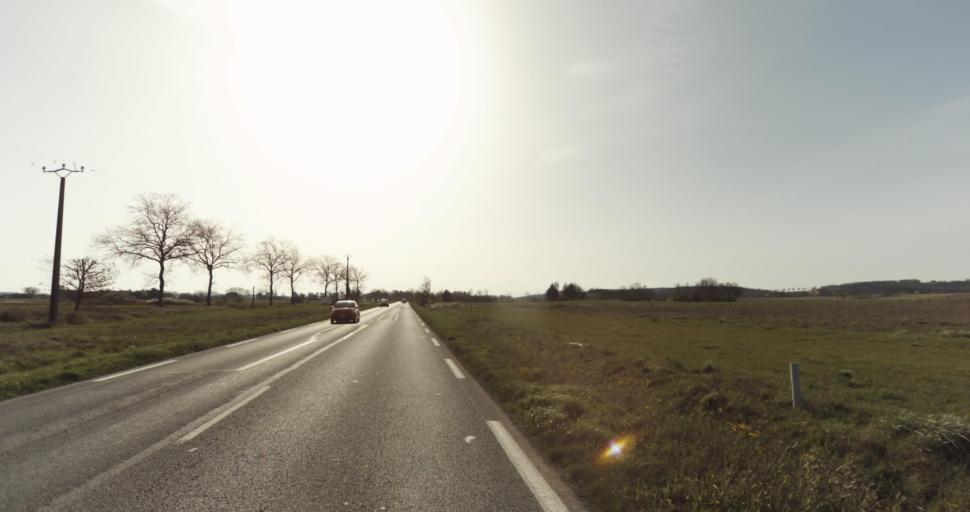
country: FR
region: Midi-Pyrenees
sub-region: Departement du Tarn
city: Saint-Sulpice-la-Pointe
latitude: 43.7543
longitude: 1.7202
